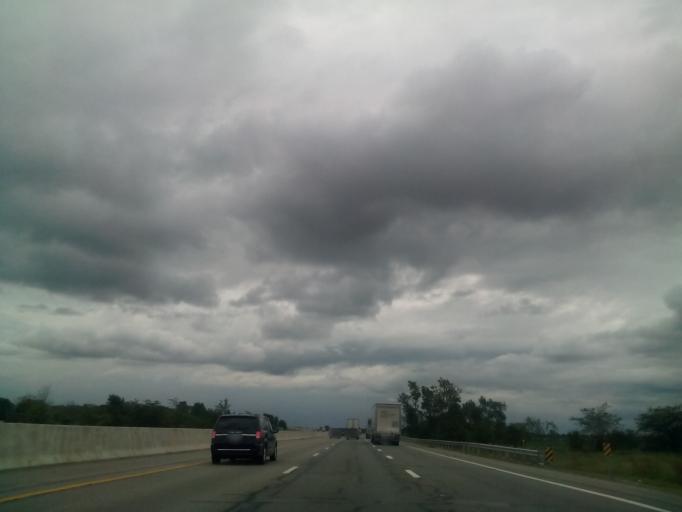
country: US
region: Ohio
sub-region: Wood County
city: Walbridge
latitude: 41.5439
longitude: -83.5269
